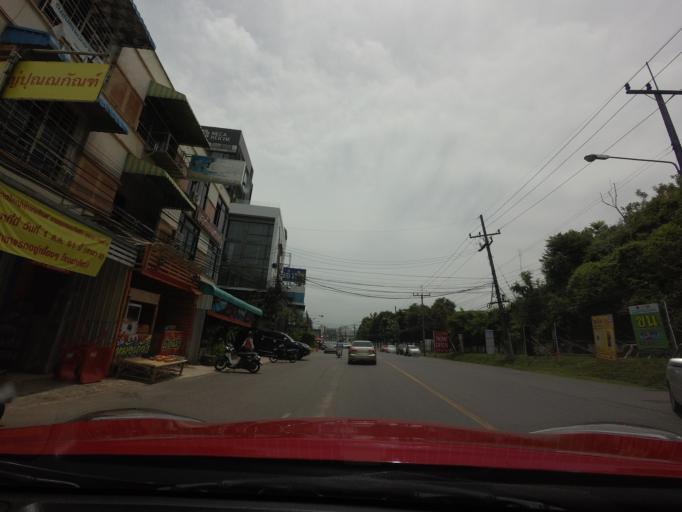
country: TH
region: Songkhla
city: Hat Yai
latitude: 6.9995
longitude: 100.5076
